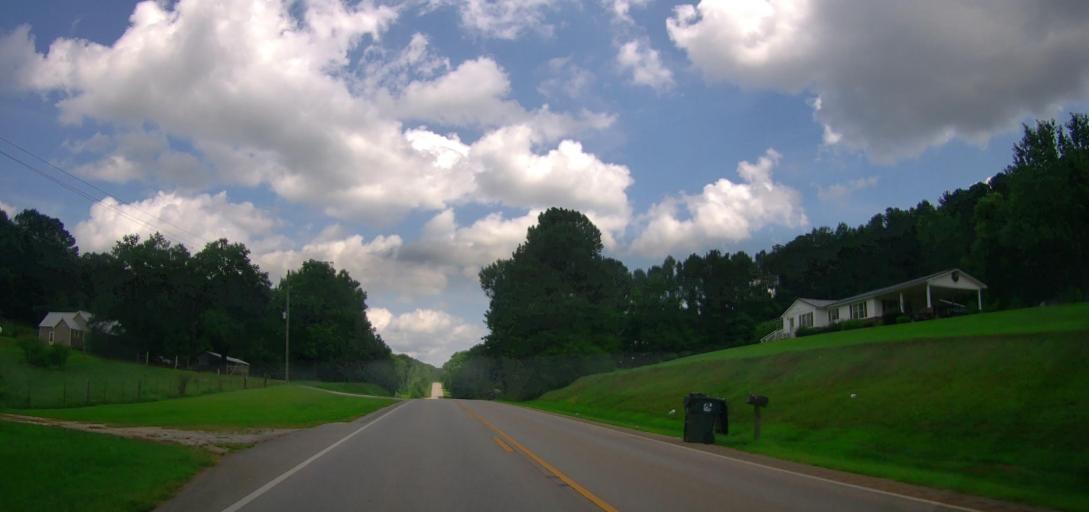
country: US
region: Georgia
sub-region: Carroll County
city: Bowdon
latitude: 33.5602
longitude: -85.4200
